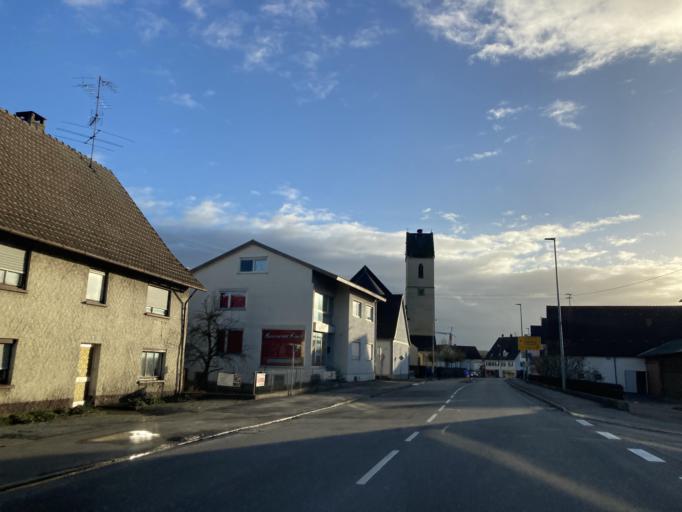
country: DE
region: Baden-Wuerttemberg
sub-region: Tuebingen Region
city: Herbertingen
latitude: 48.0623
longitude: 9.4386
